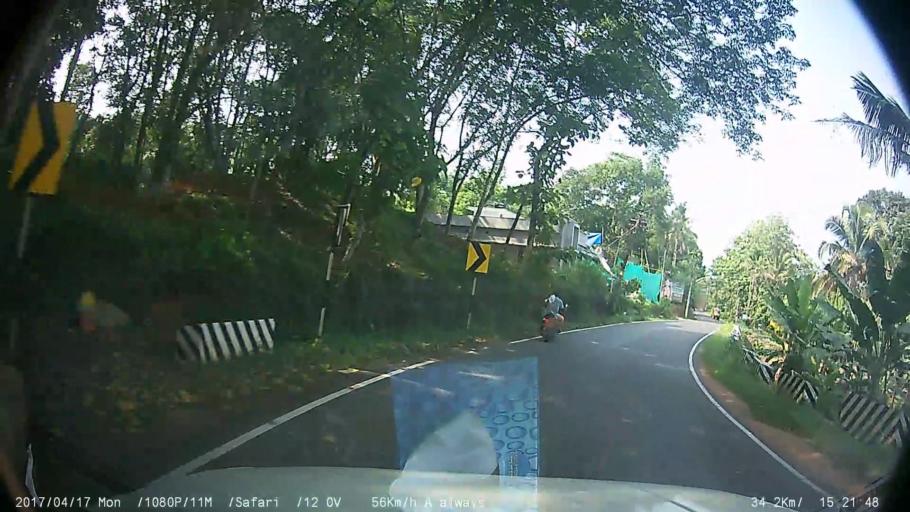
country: IN
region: Kerala
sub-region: Ernakulam
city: Ramamangalam
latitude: 9.9335
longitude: 76.4510
